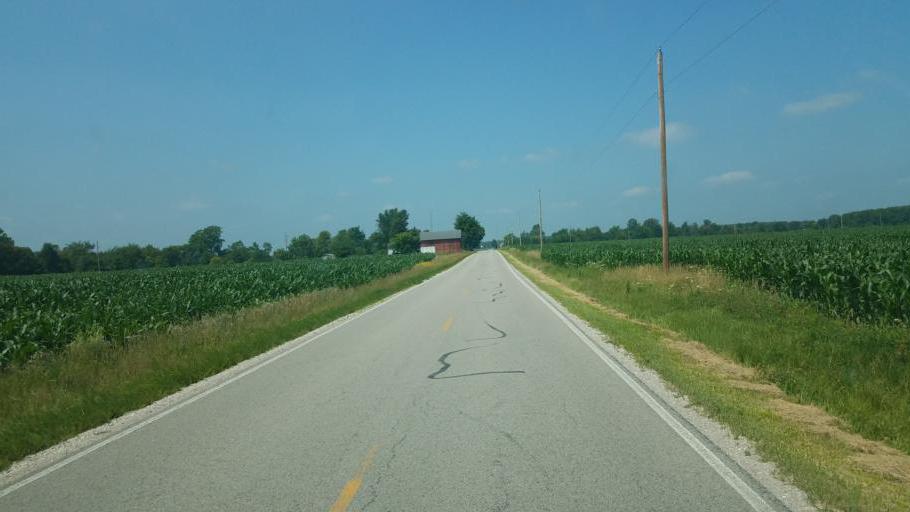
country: US
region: Ohio
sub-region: Huron County
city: Willard
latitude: 40.9937
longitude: -82.9068
